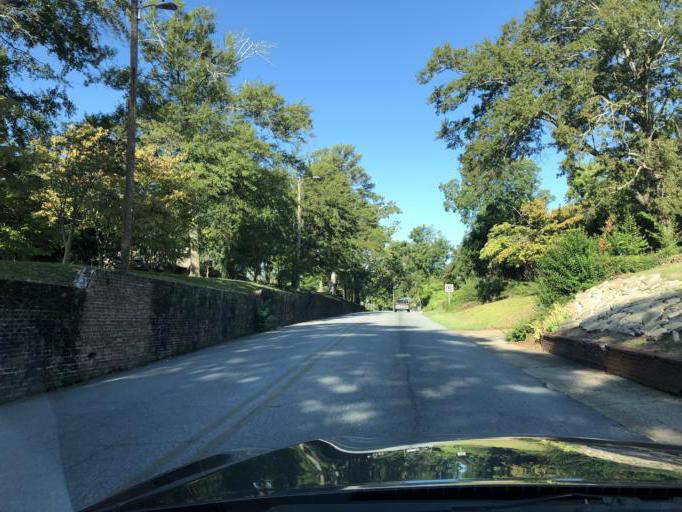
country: US
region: Georgia
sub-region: Muscogee County
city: Columbus
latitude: 32.4785
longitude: -84.9681
